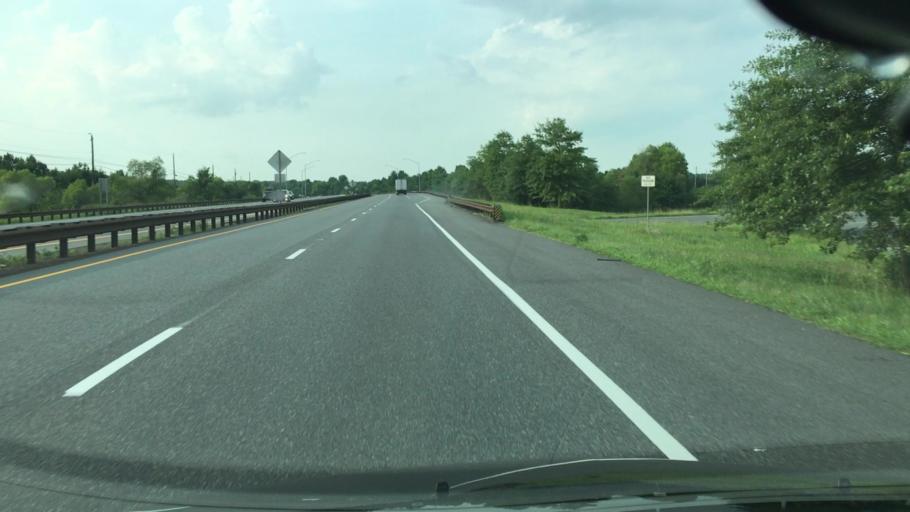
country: US
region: Delaware
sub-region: Sussex County
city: Selbyville
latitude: 38.4121
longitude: -75.2125
